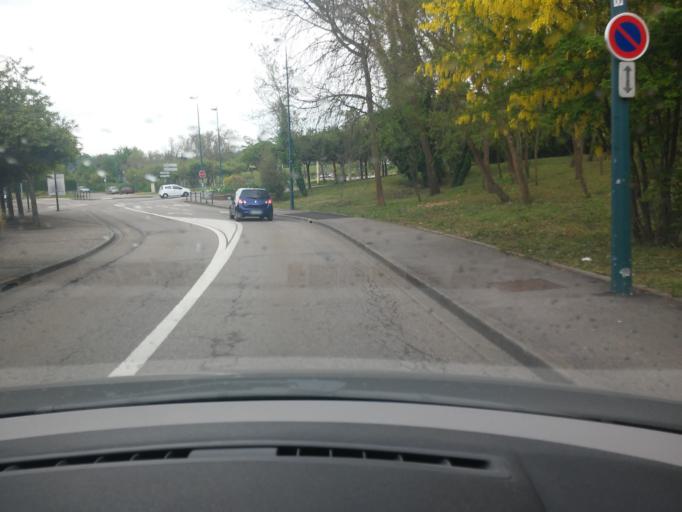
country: FR
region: Lorraine
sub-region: Departement de Meurthe-et-Moselle
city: Laxou
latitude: 48.6804
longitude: 6.1434
